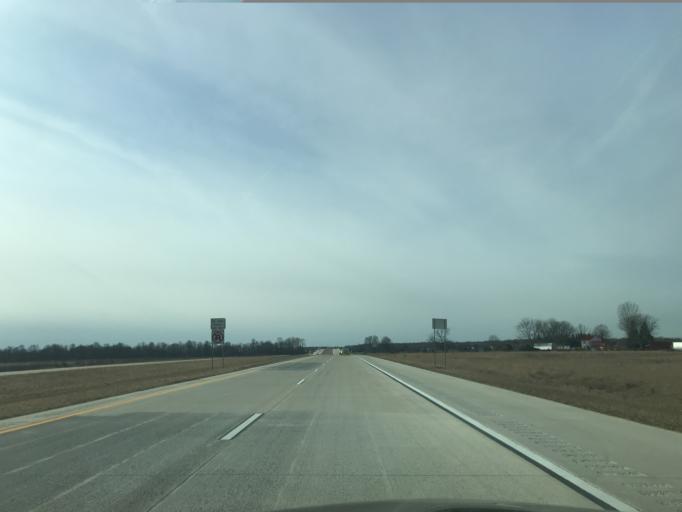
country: US
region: Delaware
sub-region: New Castle County
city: Middletown
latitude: 39.4958
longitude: -75.7037
